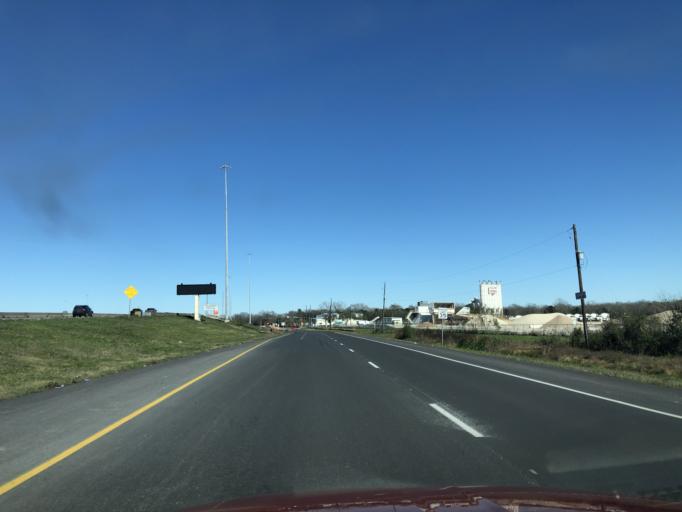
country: US
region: Texas
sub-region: Harris County
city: Southside Place
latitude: 29.6653
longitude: -95.3839
